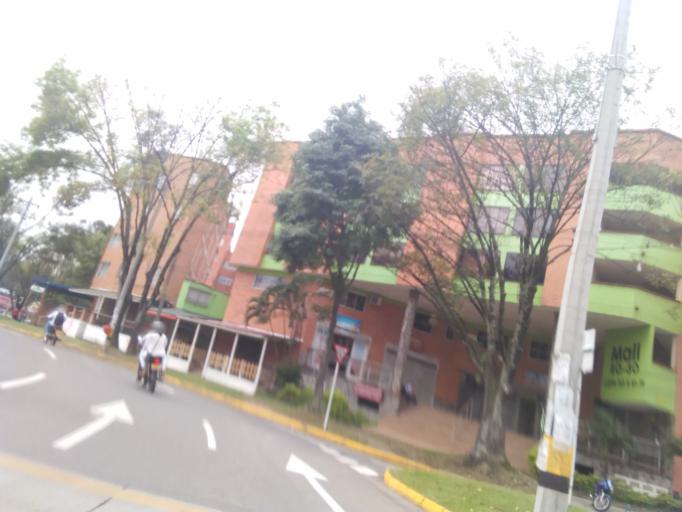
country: CO
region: Antioquia
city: Medellin
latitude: 6.2312
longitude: -75.6024
